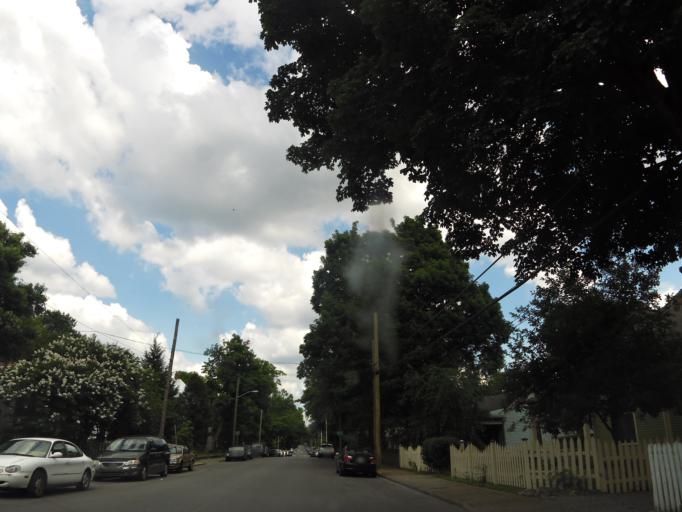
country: US
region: Tennessee
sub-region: Davidson County
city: Nashville
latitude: 36.1734
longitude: -86.7422
